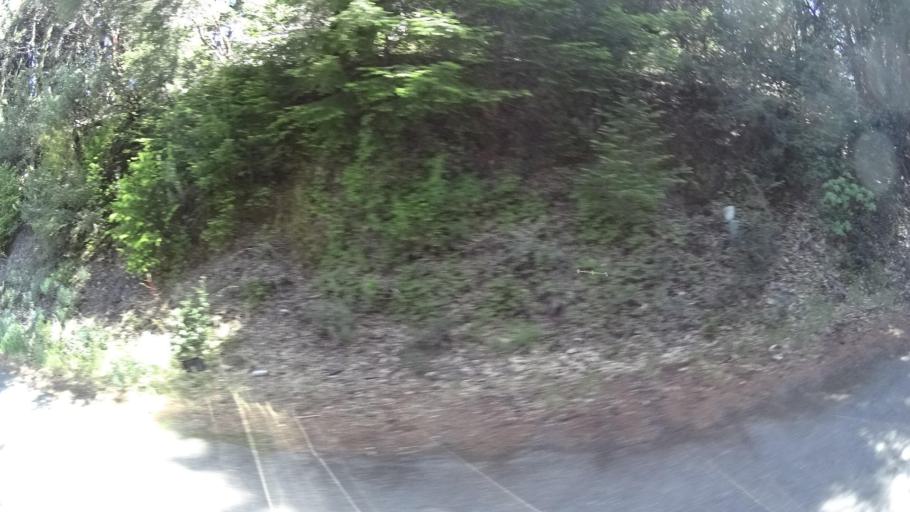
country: US
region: California
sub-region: Humboldt County
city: Redway
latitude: 40.1682
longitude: -124.0851
